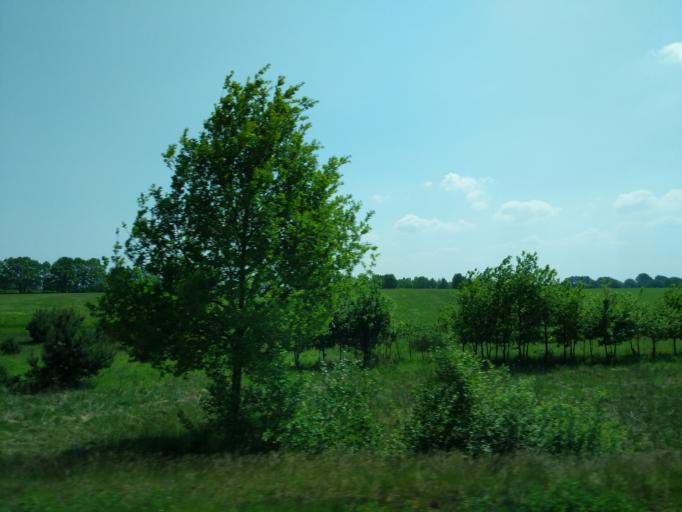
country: DE
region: Mecklenburg-Vorpommern
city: Klein Rogahn
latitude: 53.5619
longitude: 11.3592
